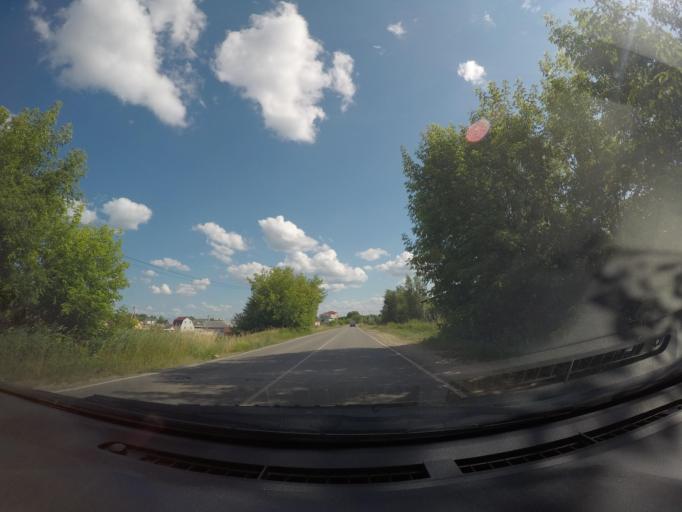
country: RU
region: Moskovskaya
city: Rechitsy
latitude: 55.5933
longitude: 38.5209
